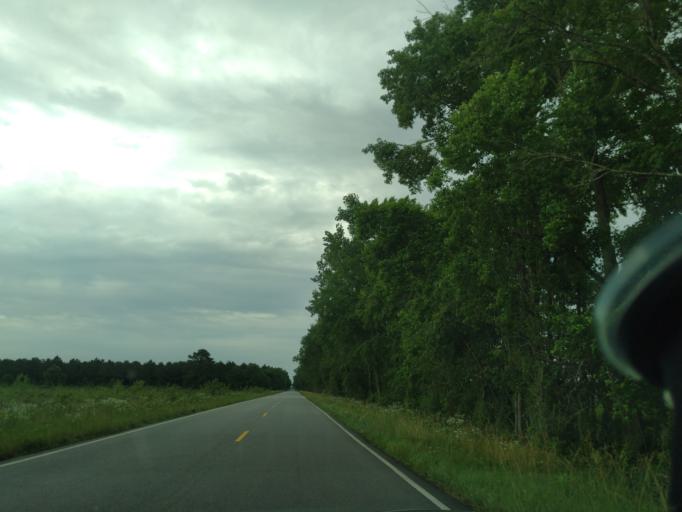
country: US
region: North Carolina
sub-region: Washington County
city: Plymouth
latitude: 35.8601
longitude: -76.5776
